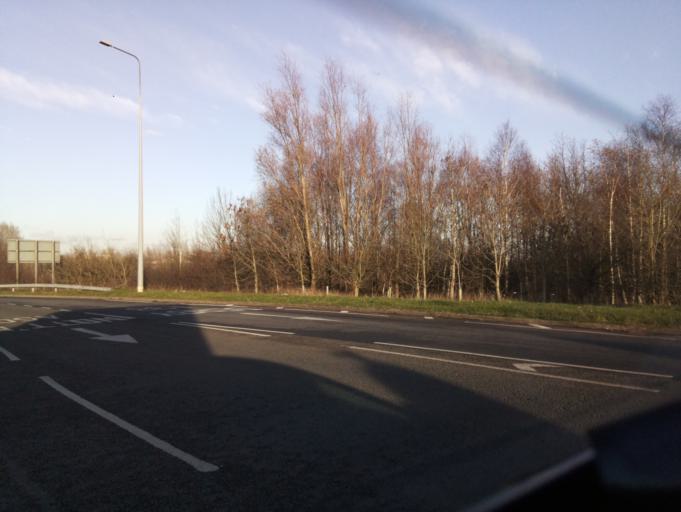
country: GB
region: England
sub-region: Derbyshire
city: Findern
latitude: 52.8676
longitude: -1.5687
